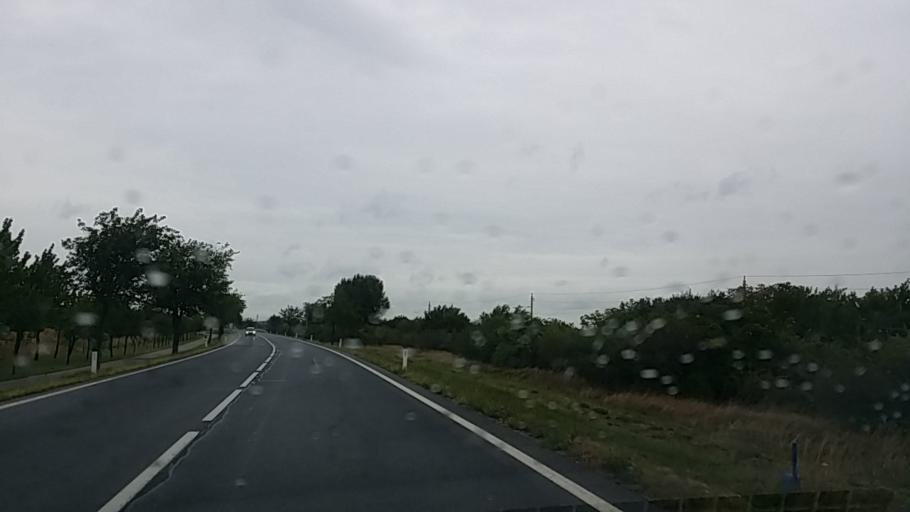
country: AT
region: Burgenland
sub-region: Eisenstadt-Umgebung
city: Schutzen am Gebirge
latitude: 47.8594
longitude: 16.6406
